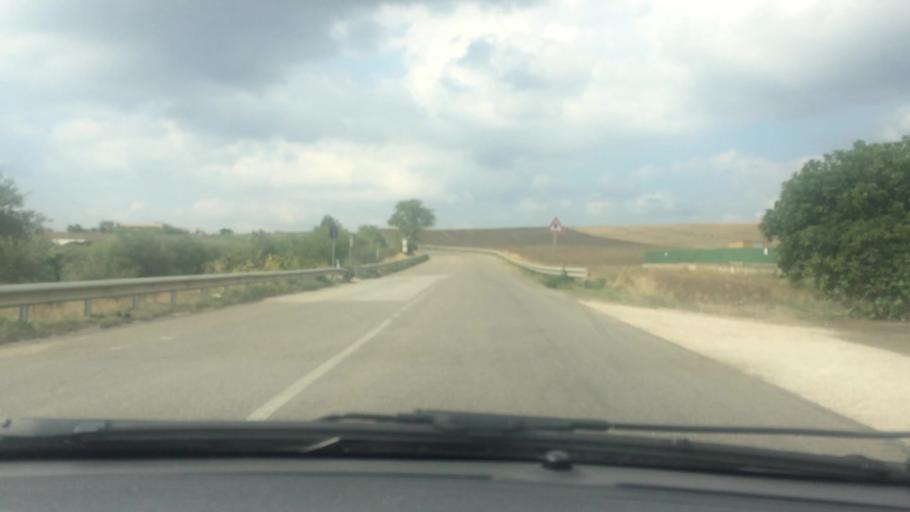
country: IT
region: Basilicate
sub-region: Provincia di Matera
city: La Martella
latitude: 40.6882
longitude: 16.5601
